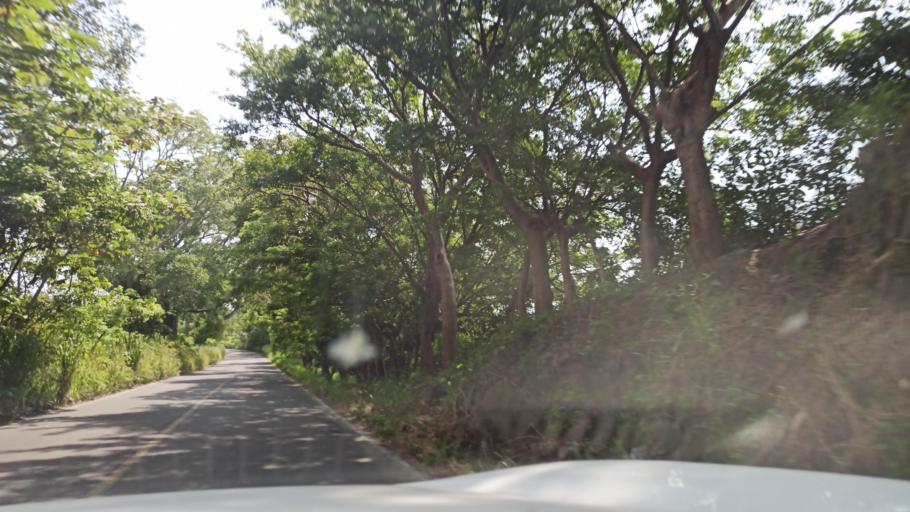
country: MX
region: Veracruz
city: Martinez de la Torre
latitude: 20.0862
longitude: -97.0780
